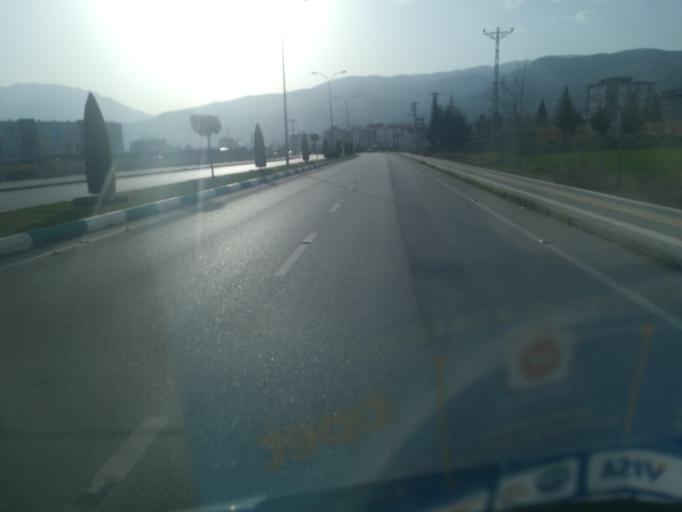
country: TR
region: Osmaniye
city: Osmaniye
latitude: 37.0512
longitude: 36.2263
